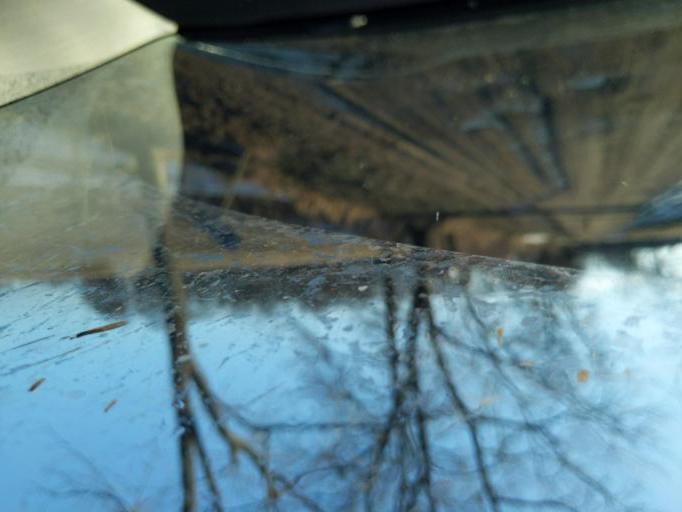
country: US
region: Michigan
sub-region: Ingham County
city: Stockbridge
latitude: 42.5264
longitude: -84.2600
